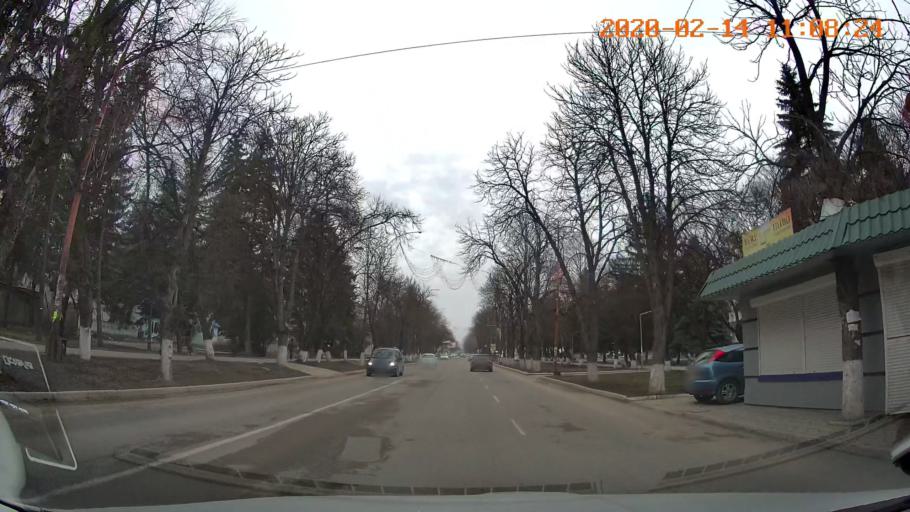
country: MD
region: Raionul Edinet
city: Edinet
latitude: 48.1718
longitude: 27.3025
